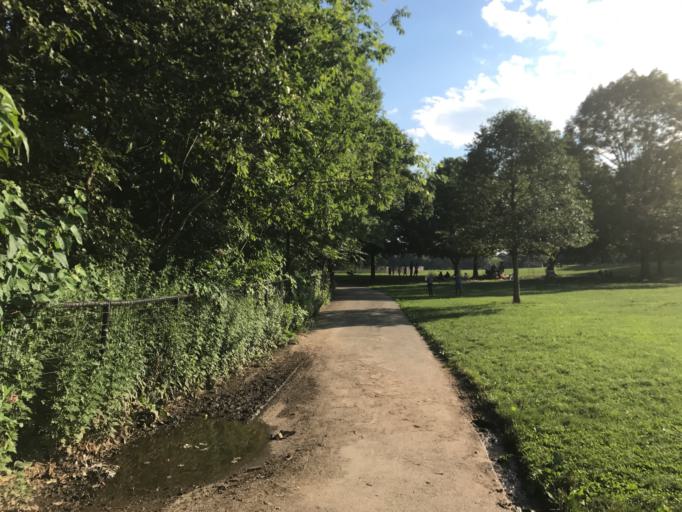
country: US
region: New York
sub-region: Kings County
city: Brooklyn
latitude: 40.6637
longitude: -73.9715
